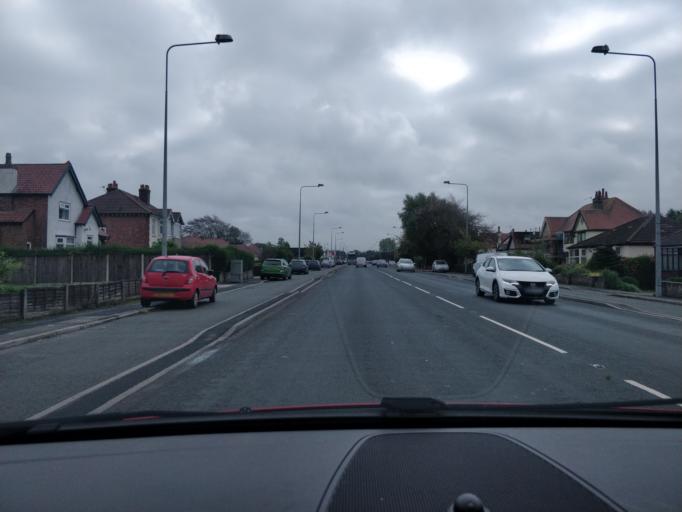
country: GB
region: England
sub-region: Sefton
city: Southport
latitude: 53.6300
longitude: -2.9669
